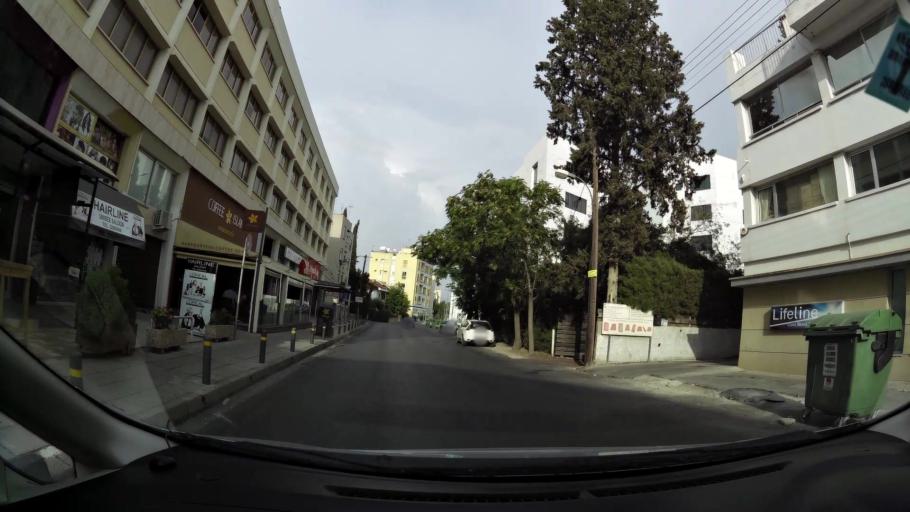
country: CY
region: Lefkosia
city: Nicosia
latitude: 35.1616
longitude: 33.3456
